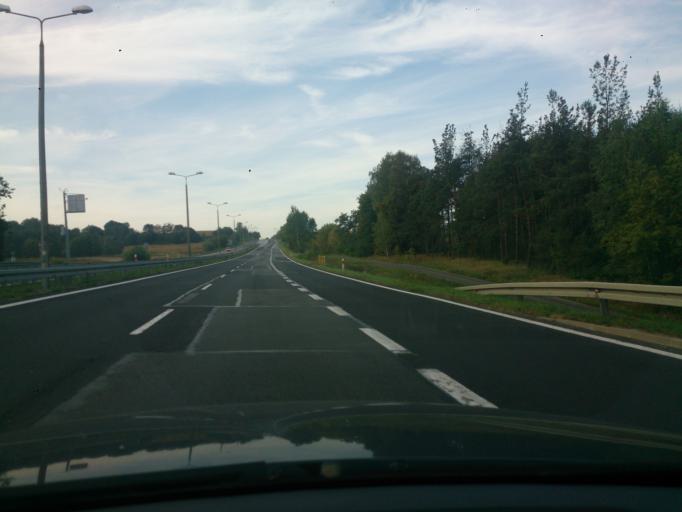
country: PL
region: Kujawsko-Pomorskie
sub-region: Powiat chelminski
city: Chelmno
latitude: 53.3756
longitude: 18.3408
